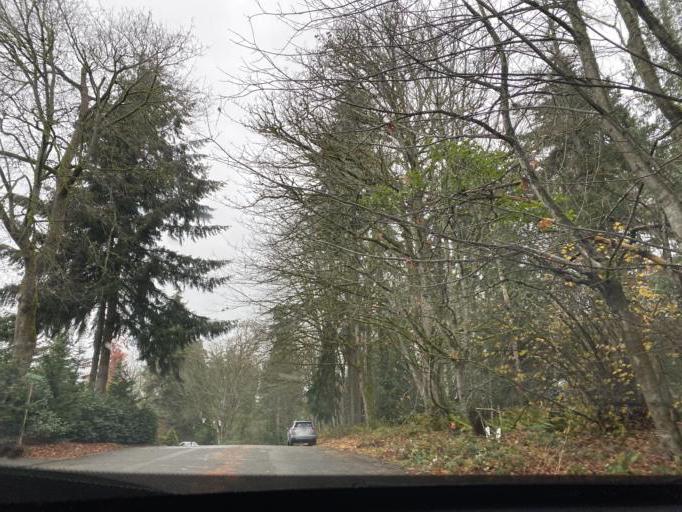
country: US
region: Washington
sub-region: King County
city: Mercer Island
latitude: 47.5515
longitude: -122.2269
